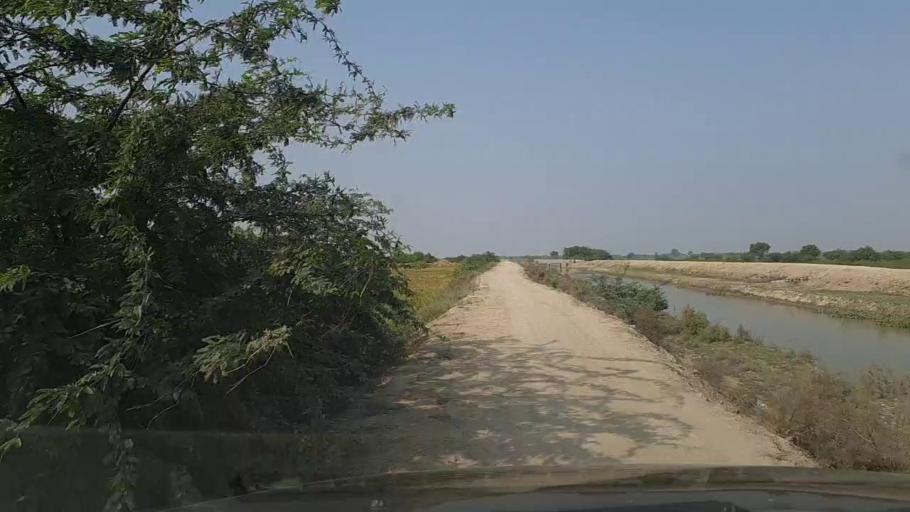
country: PK
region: Sindh
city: Mirpur Batoro
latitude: 24.6845
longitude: 68.2478
